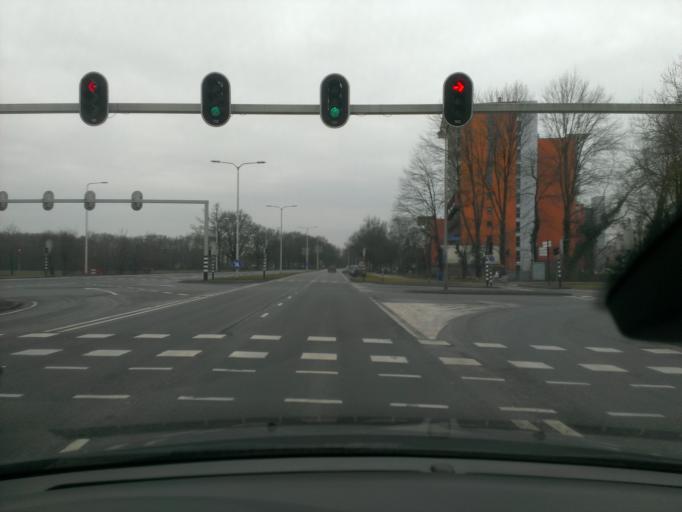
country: NL
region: Overijssel
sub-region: Gemeente Almelo
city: Almelo
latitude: 52.3567
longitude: 6.6744
